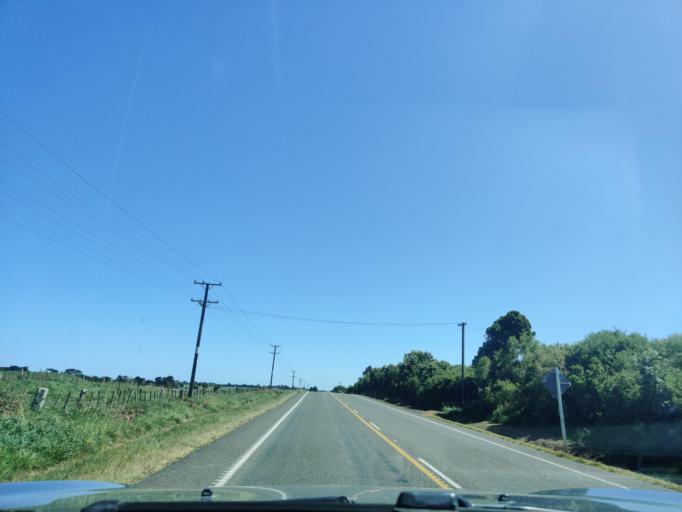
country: NZ
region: Taranaki
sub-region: South Taranaki District
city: Patea
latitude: -39.7729
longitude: 174.6741
